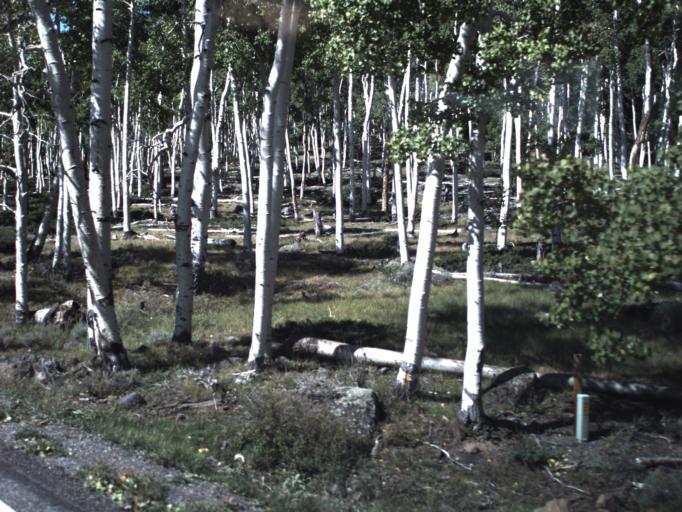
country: US
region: Utah
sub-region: Wayne County
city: Loa
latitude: 38.5287
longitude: -111.7463
